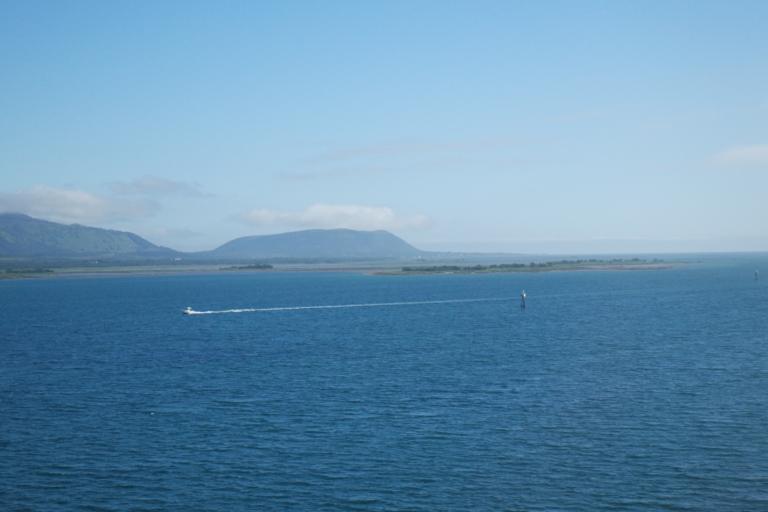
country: NO
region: Nordland
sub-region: Sortland
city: Sortland
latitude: 68.9656
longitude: 15.6347
